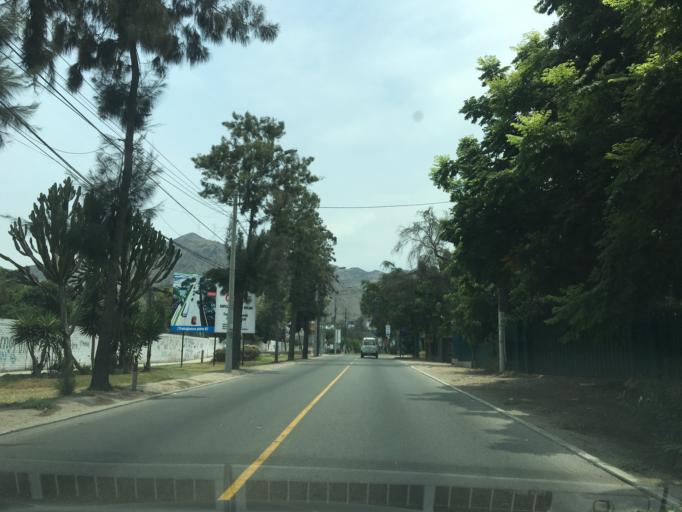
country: PE
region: Lima
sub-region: Lima
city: La Molina
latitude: -12.0765
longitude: -76.9411
